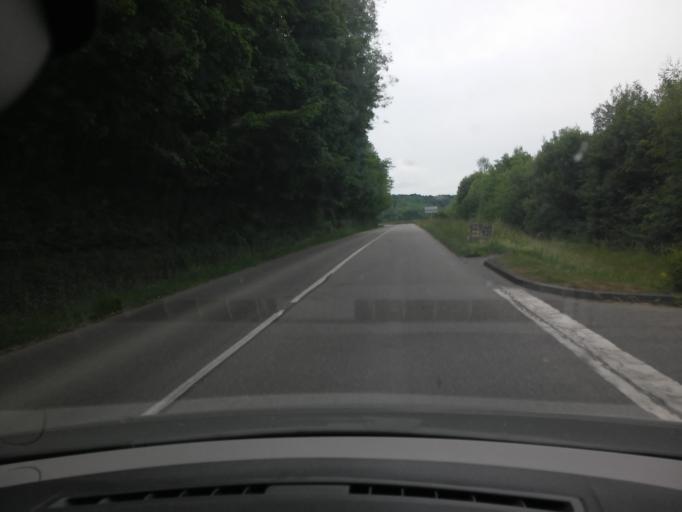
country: FR
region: Lorraine
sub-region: Departement de la Meuse
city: Commercy
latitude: 48.7698
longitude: 5.5771
